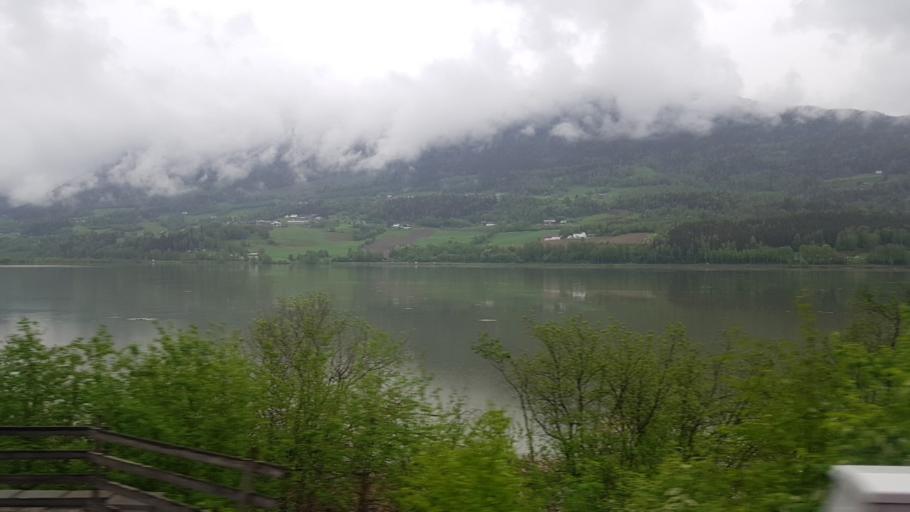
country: NO
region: Oppland
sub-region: Ringebu
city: Ringebu
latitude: 61.4545
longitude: 10.2042
